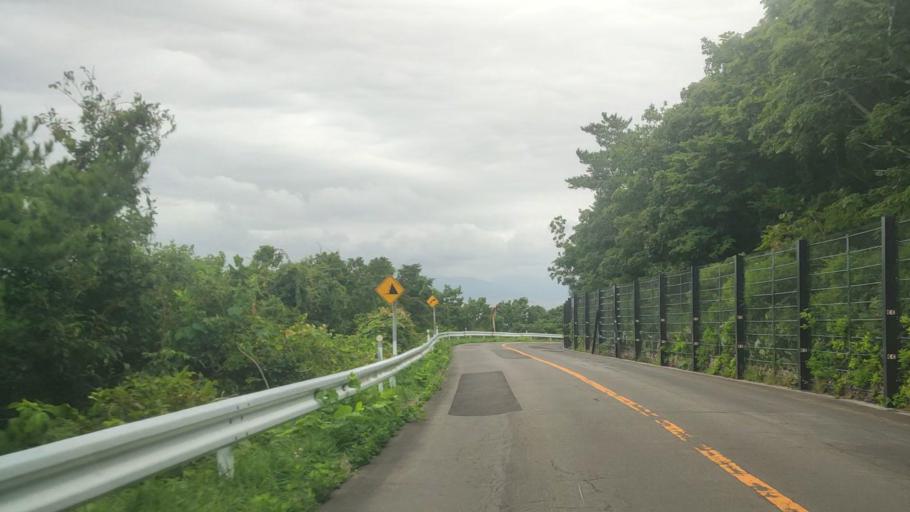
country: JP
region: Hokkaido
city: Hakodate
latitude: 41.7616
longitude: 140.6990
